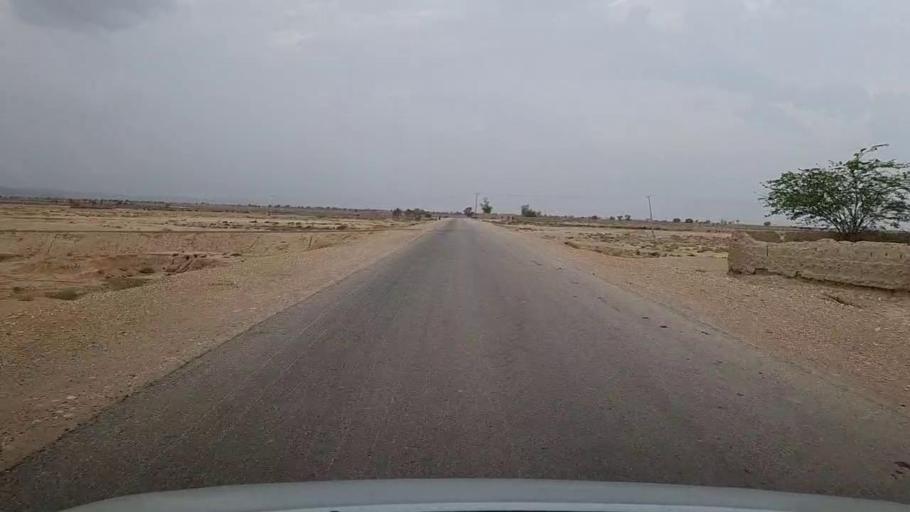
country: PK
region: Sindh
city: Sehwan
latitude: 26.3365
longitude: 67.7159
